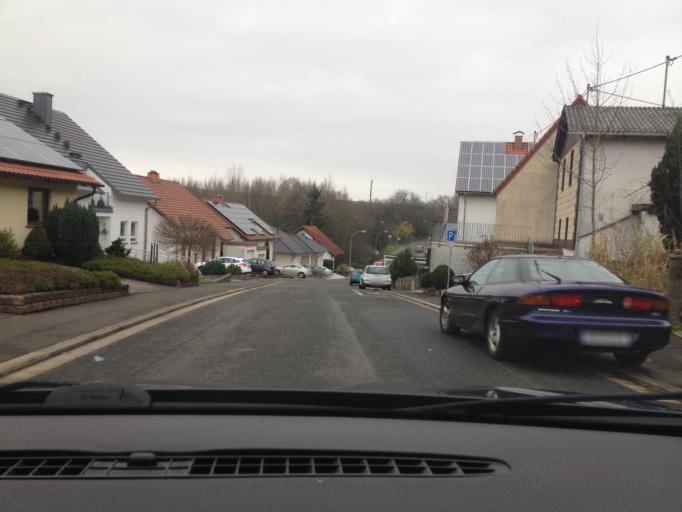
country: DE
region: Saarland
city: Schiffweiler
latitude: 49.3646
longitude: 7.1387
